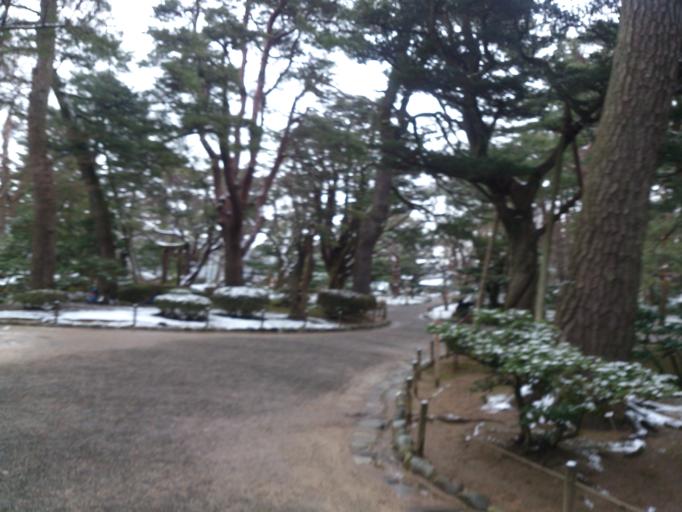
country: JP
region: Ishikawa
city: Kanazawa-shi
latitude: 36.5615
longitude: 136.6634
